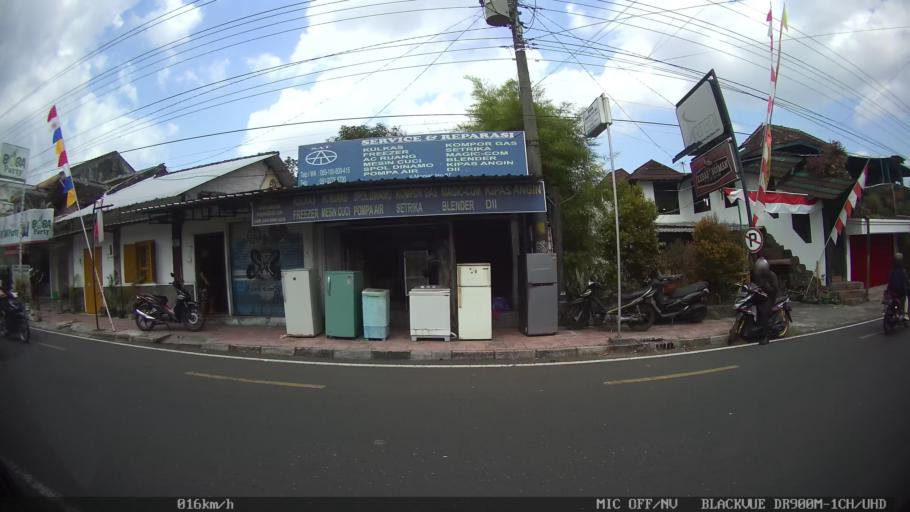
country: ID
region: Daerah Istimewa Yogyakarta
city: Melati
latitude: -7.7581
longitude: 110.3698
